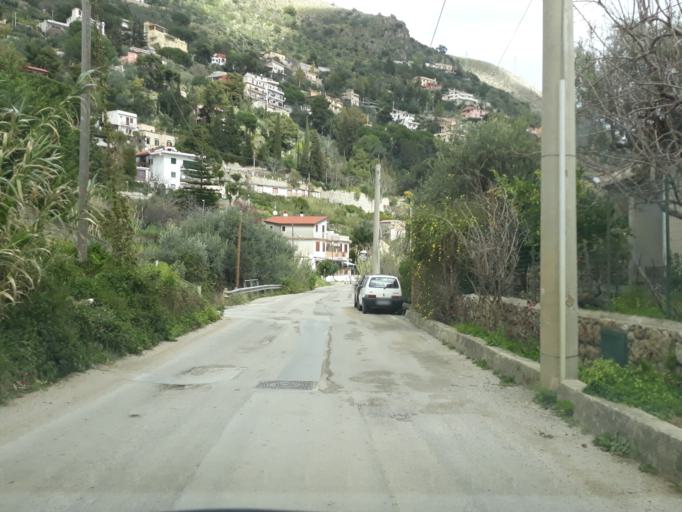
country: IT
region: Sicily
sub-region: Palermo
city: Monreale
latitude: 38.0852
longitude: 13.2979
